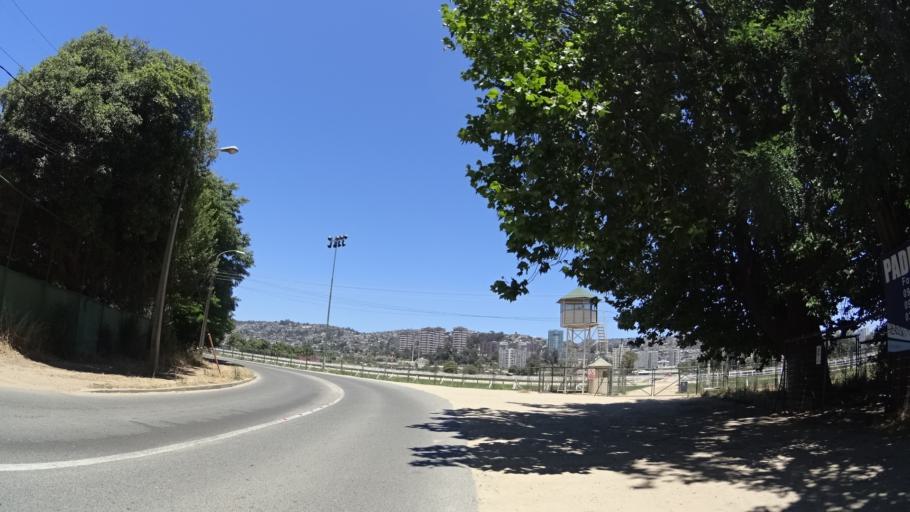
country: CL
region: Valparaiso
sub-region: Provincia de Valparaiso
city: Vina del Mar
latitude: -33.0226
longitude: -71.5353
